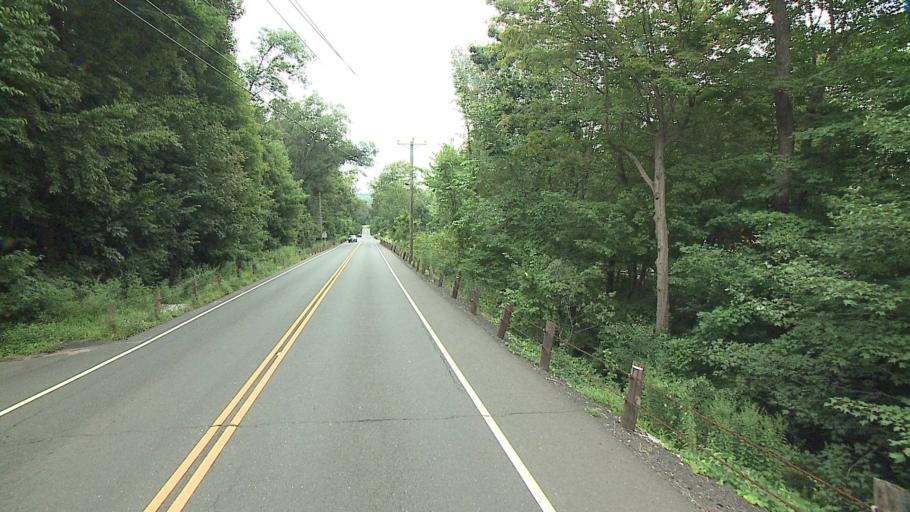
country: US
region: Connecticut
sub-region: New Haven County
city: Middlebury
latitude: 41.5286
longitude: -73.1285
